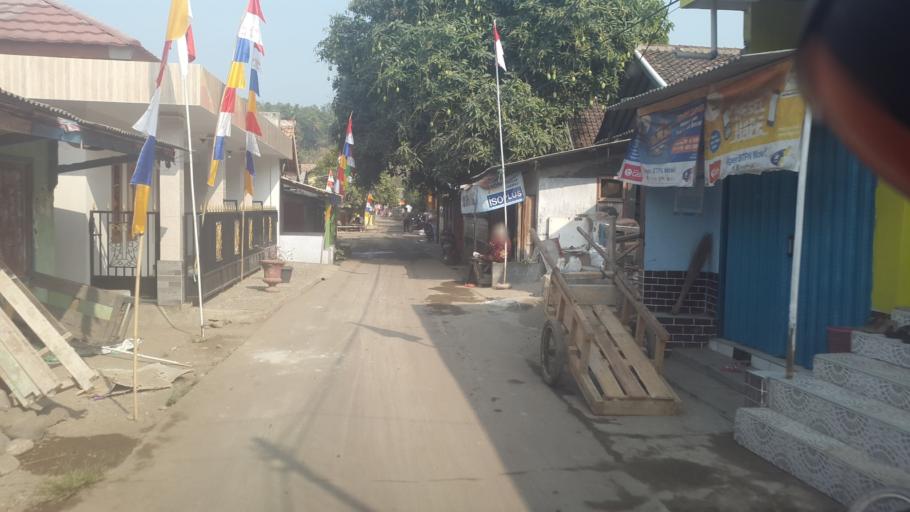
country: ID
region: West Java
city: Tugu
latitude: -6.9522
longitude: 106.4421
